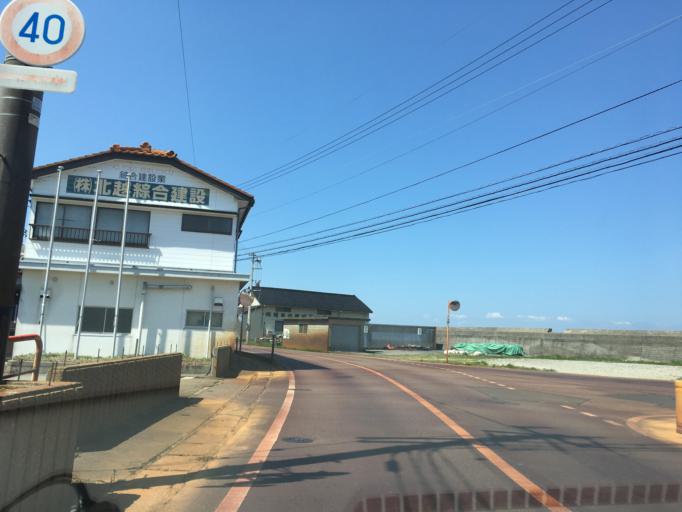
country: JP
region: Toyama
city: Kuragaki-kosugi
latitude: 36.7567
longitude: 137.1903
